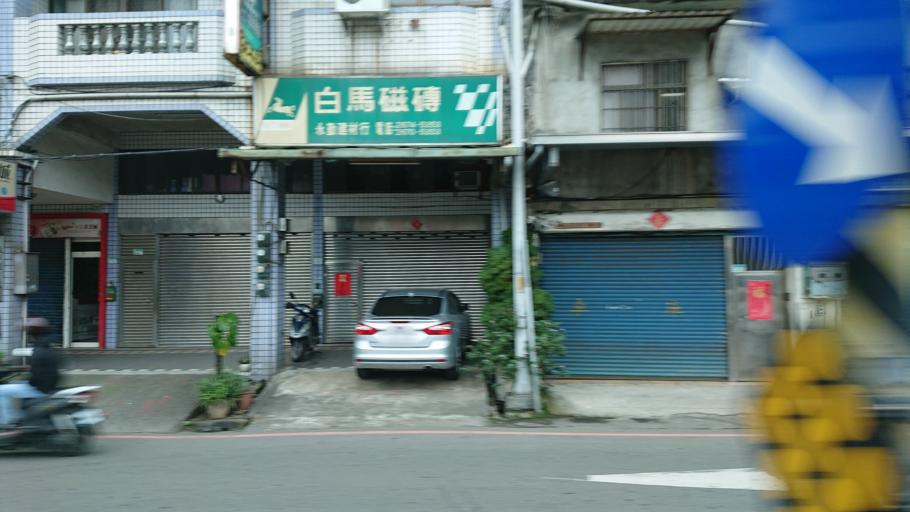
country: TW
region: Taiwan
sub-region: Taoyuan
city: Taoyuan
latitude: 24.9570
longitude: 121.3515
